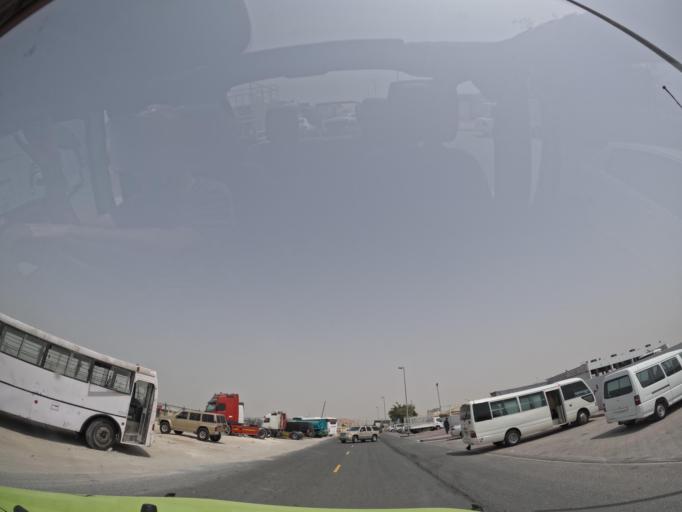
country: AE
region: Ash Shariqah
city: Sharjah
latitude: 25.1880
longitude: 55.3767
